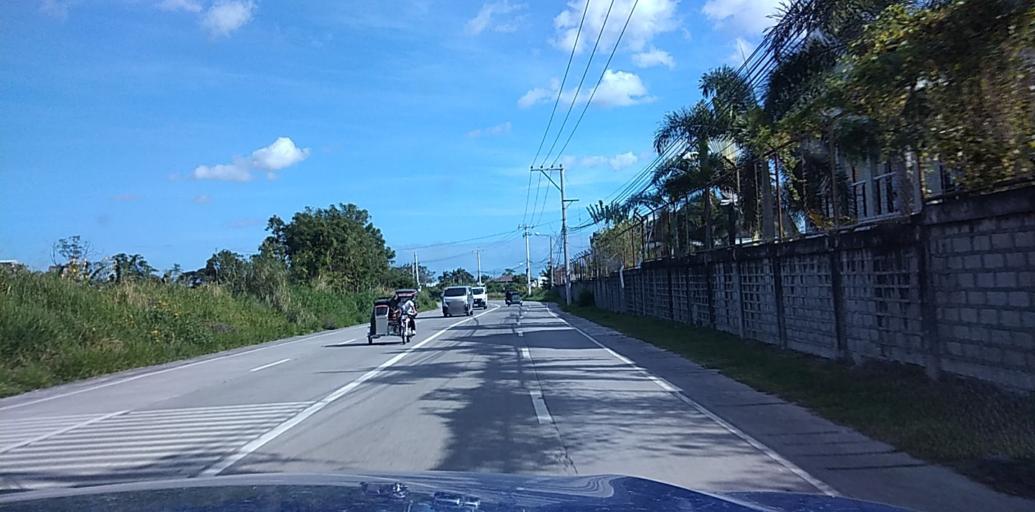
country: PH
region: Central Luzon
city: Santol
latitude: 15.1448
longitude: 120.5556
